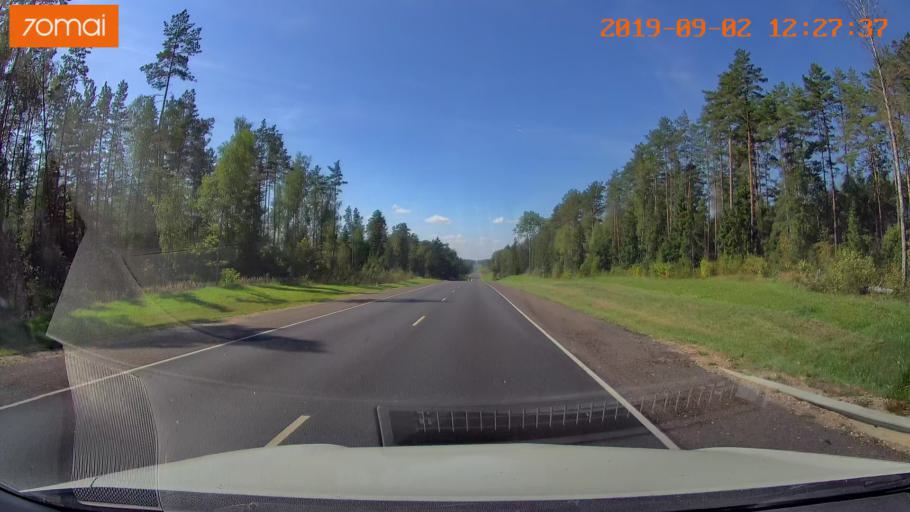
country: RU
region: Smolensk
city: Shumyachi
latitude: 53.8522
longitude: 32.5395
